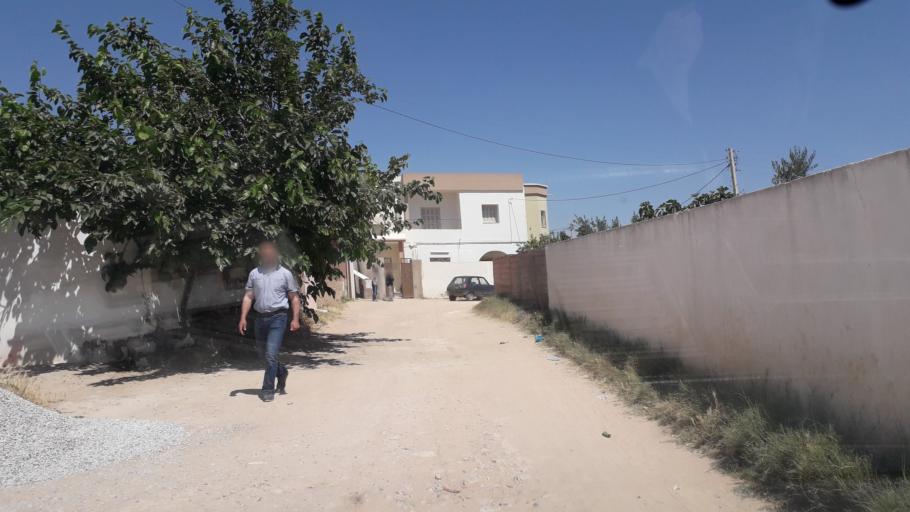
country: TN
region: Safaqis
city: Al Qarmadah
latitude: 34.8226
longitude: 10.7669
